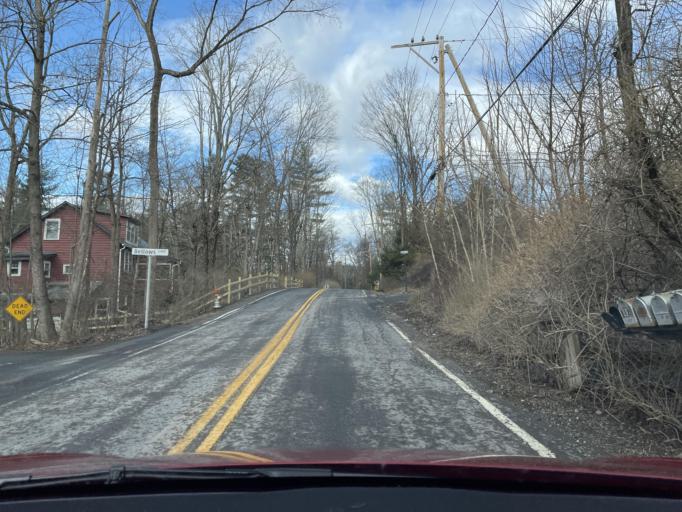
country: US
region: New York
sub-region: Ulster County
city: Woodstock
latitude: 42.0467
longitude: -74.1204
